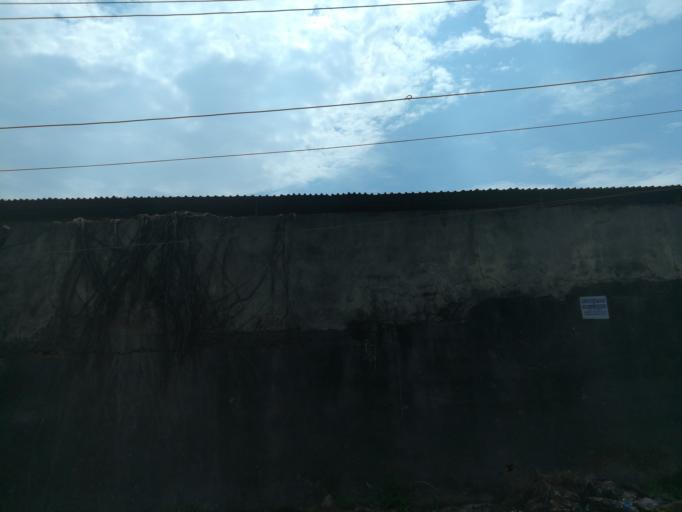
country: NG
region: Lagos
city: Oshodi
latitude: 6.5446
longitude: 3.3297
